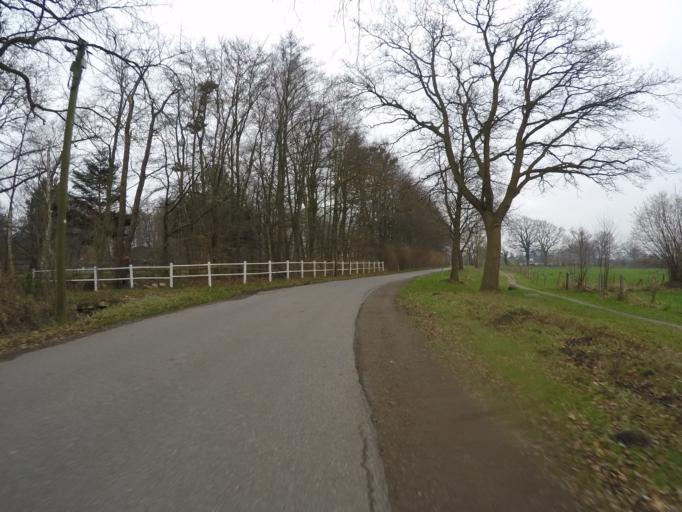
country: DE
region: Schleswig-Holstein
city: Tangstedt
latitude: 53.6898
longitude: 9.8555
